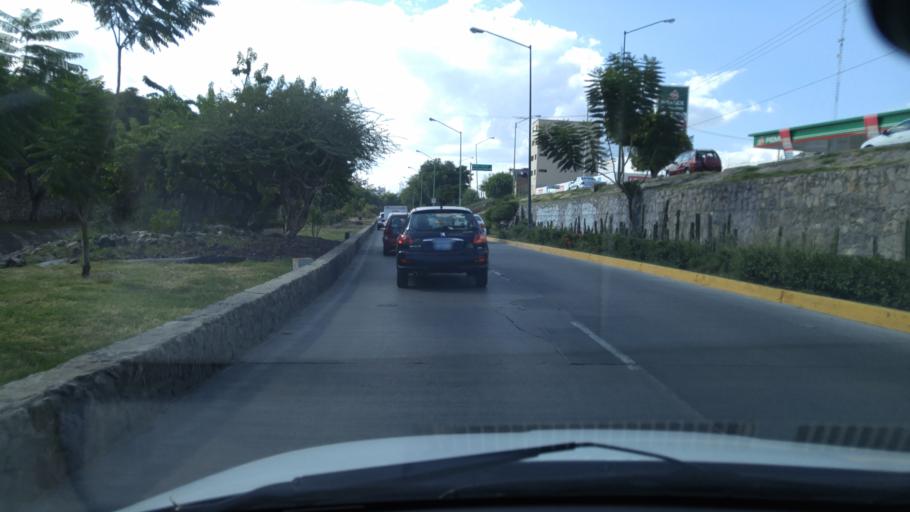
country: MX
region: Guanajuato
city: Leon
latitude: 21.1193
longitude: -101.6687
